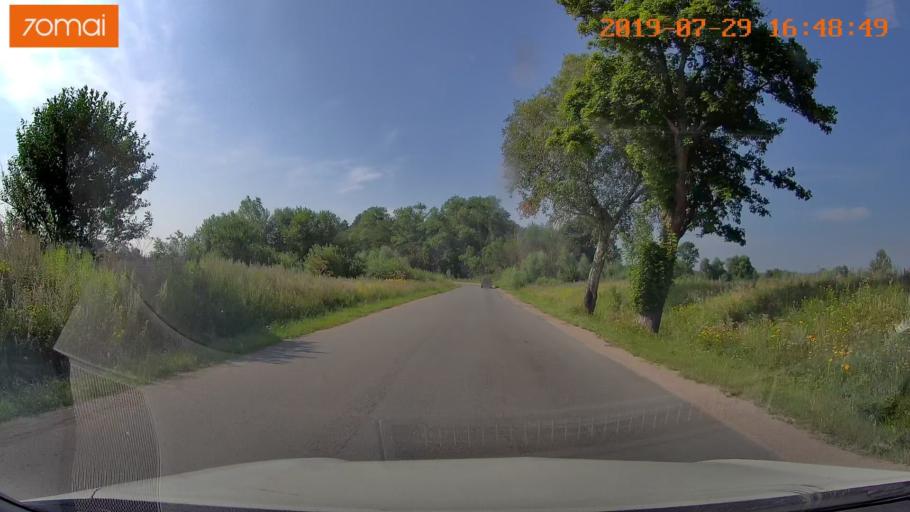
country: RU
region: Kaliningrad
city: Primorsk
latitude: 54.7898
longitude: 20.0726
